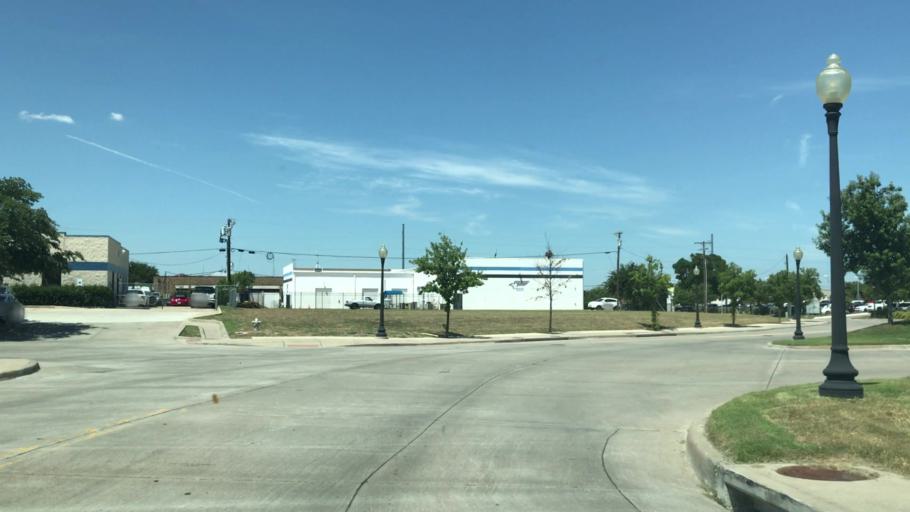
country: US
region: Texas
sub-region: Dallas County
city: Rowlett
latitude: 32.9047
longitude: -96.5644
